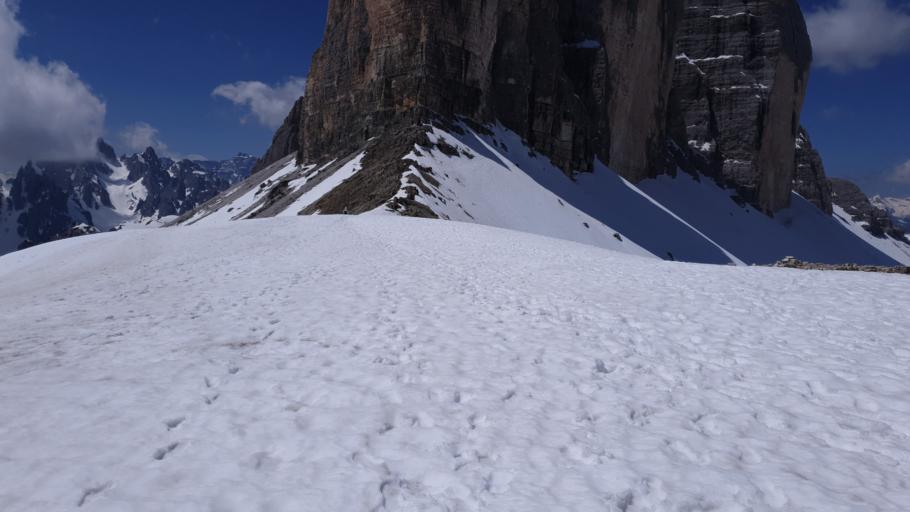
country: IT
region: Trentino-Alto Adige
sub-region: Bolzano
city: Sesto
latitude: 46.6226
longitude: 12.3118
